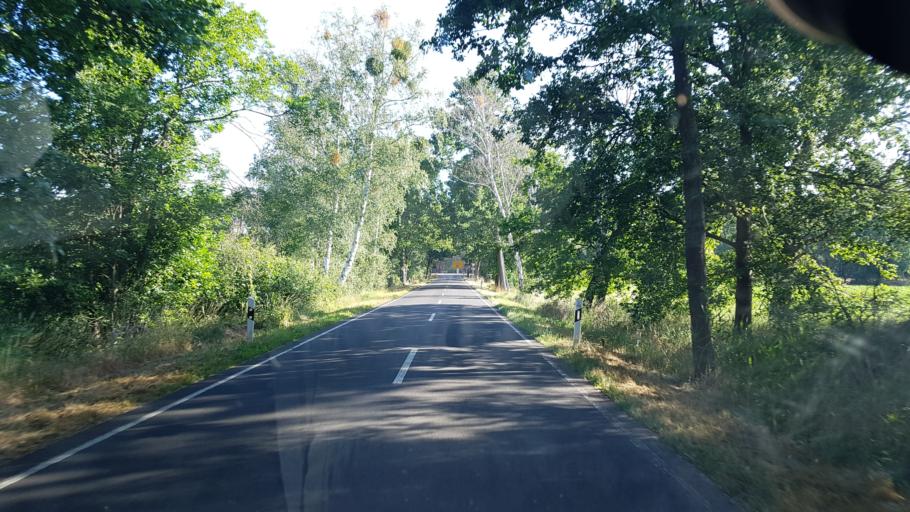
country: DE
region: Brandenburg
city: Kasel-Golzig
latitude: 51.9680
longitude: 13.6764
